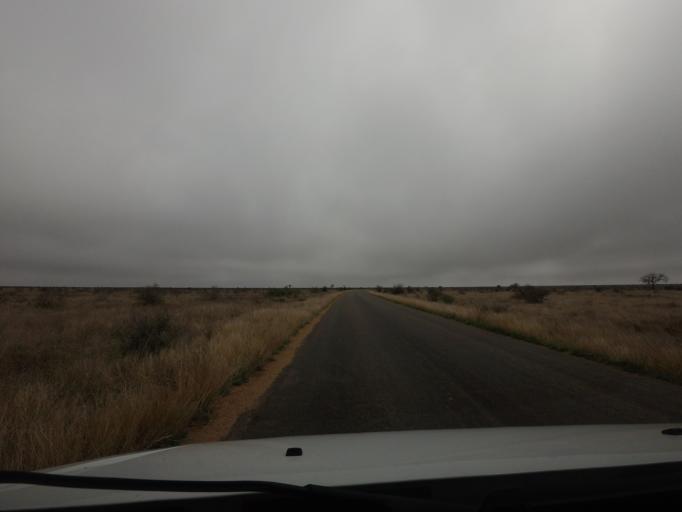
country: ZA
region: Limpopo
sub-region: Mopani District Municipality
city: Phalaborwa
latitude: -24.2394
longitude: 31.7199
